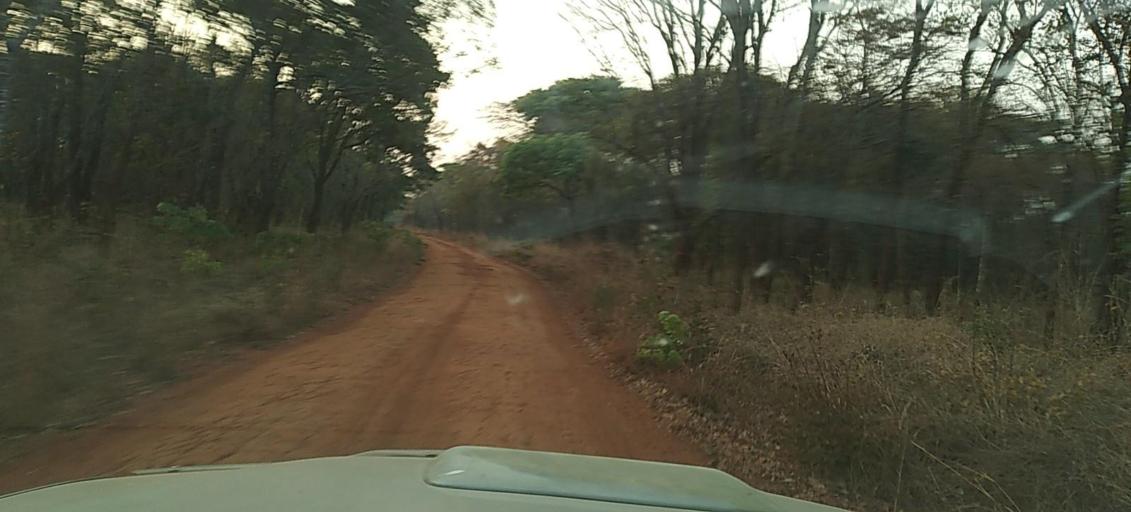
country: ZM
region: North-Western
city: Kasempa
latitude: -13.0805
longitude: 26.3939
